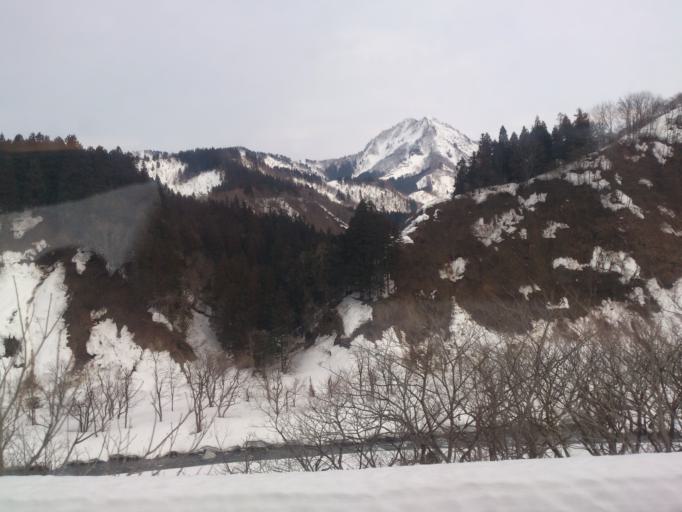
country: JP
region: Niigata
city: Shiozawa
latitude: 36.9675
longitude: 138.8026
